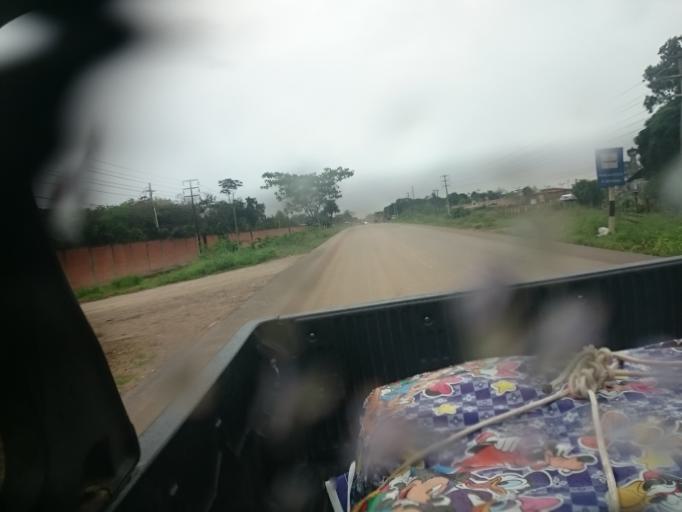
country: PE
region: Ucayali
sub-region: Provincia de Coronel Portillo
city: Puerto Callao
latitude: -8.4049
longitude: -74.6311
